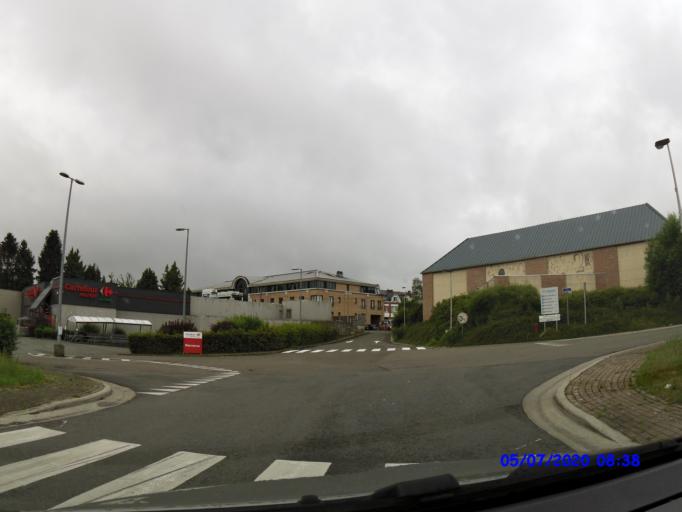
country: BE
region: Wallonia
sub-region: Province du Brabant Wallon
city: Genappe
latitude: 50.6147
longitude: 4.4540
